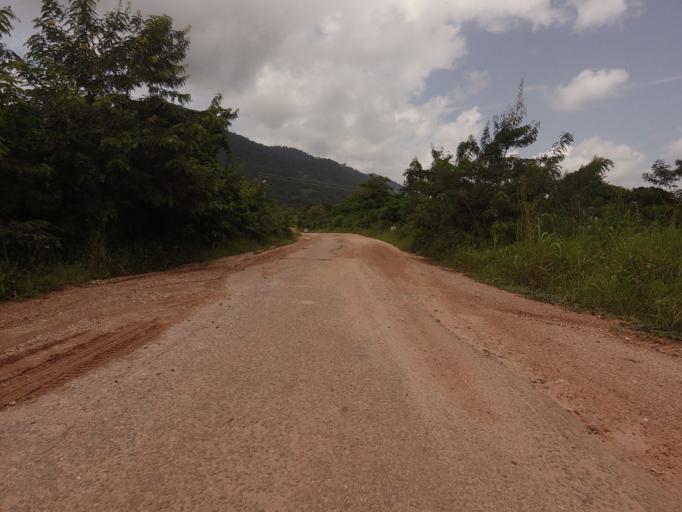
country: GH
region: Volta
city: Ho
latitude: 6.7680
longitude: 0.3639
